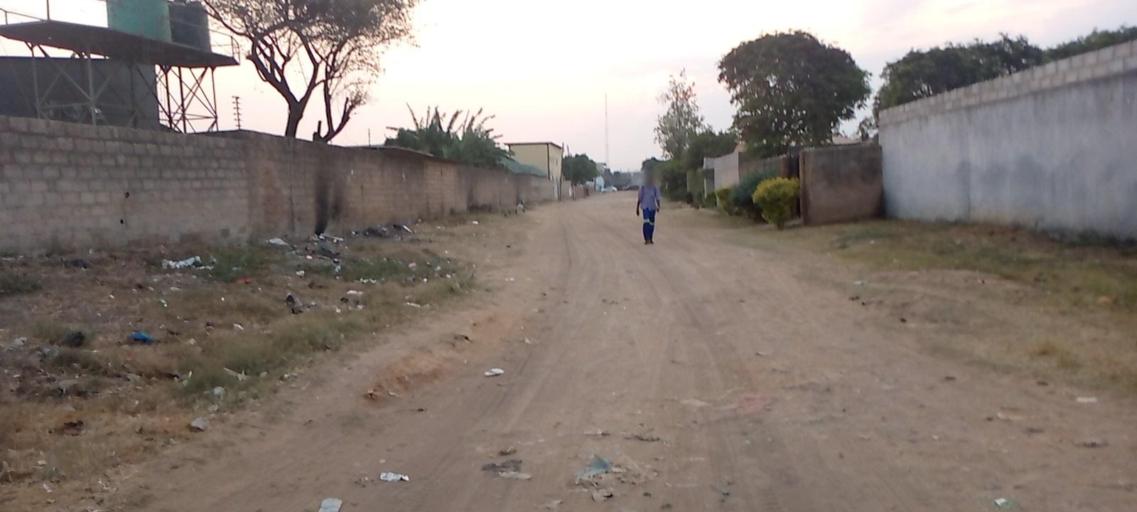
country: ZM
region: Lusaka
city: Lusaka
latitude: -15.4074
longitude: 28.3480
